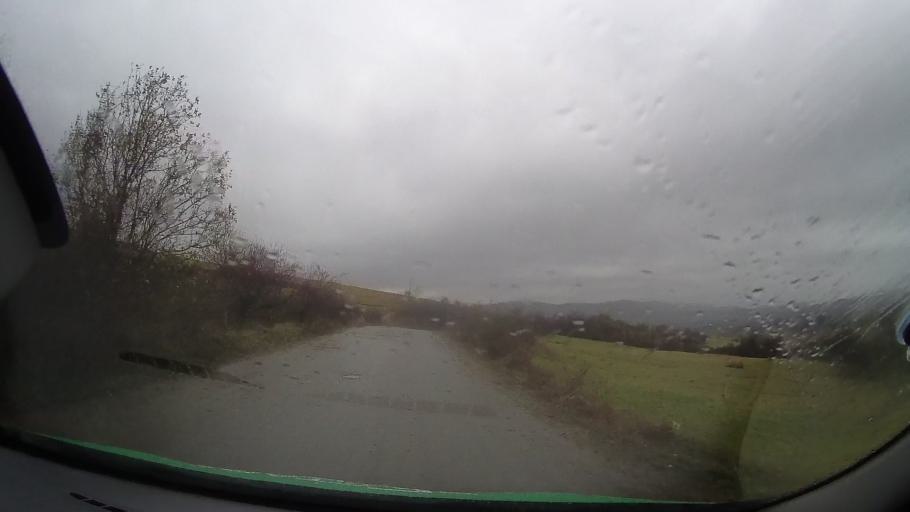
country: RO
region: Mures
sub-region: Comuna Vatava
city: Vatava
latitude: 46.9495
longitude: 24.7336
